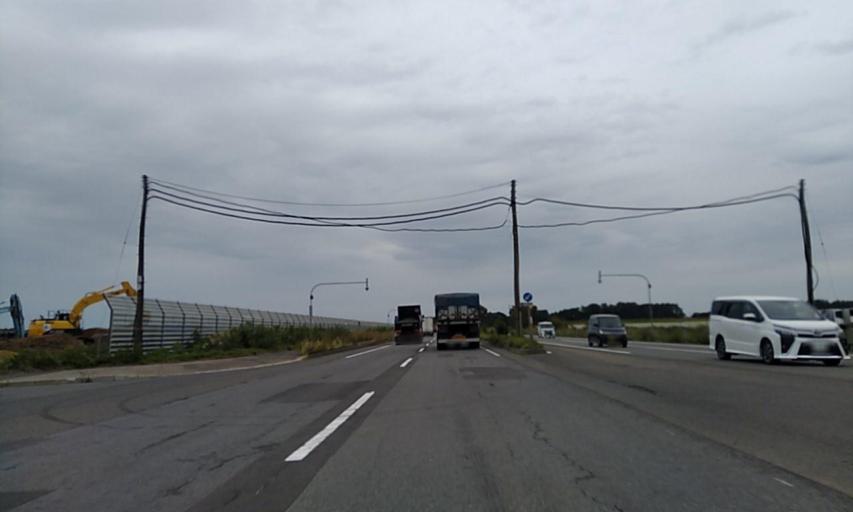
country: JP
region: Hokkaido
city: Sapporo
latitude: 43.1560
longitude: 141.2423
